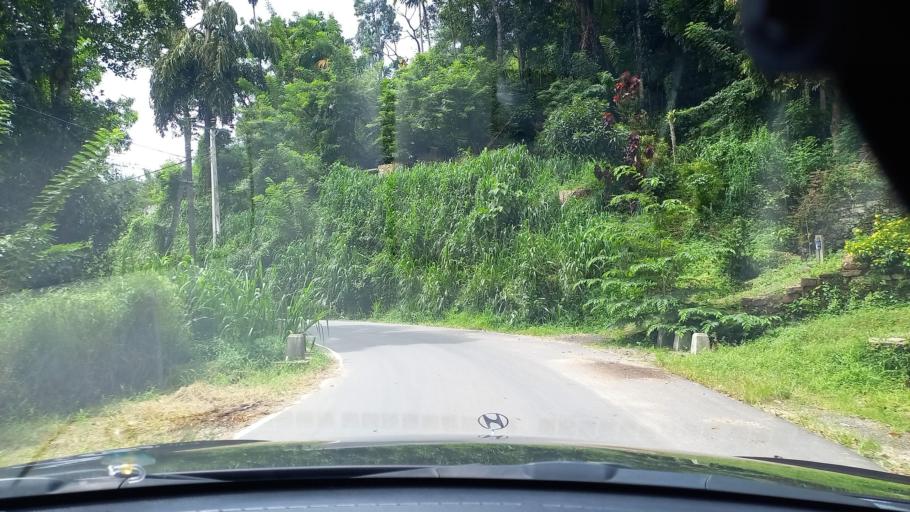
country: LK
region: Central
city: Gampola
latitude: 7.2169
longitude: 80.6144
